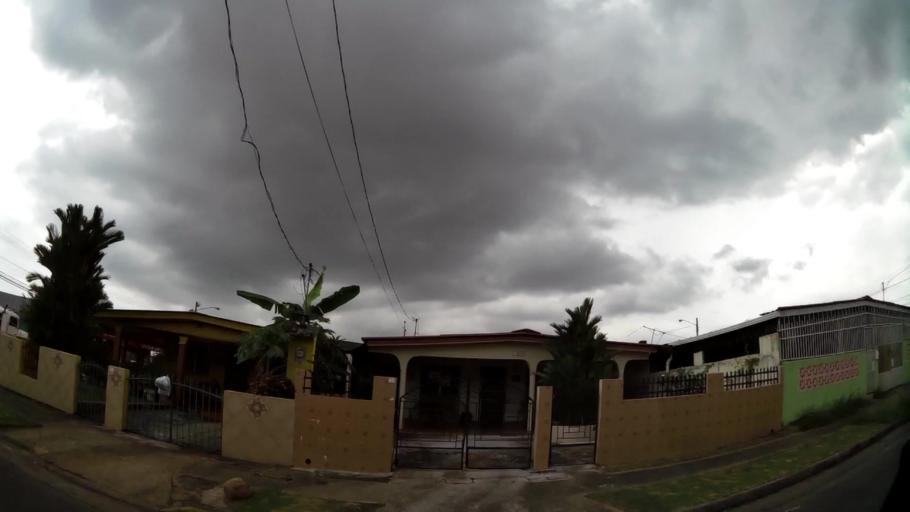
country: PA
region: Panama
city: Tocumen
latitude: 9.0522
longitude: -79.4133
